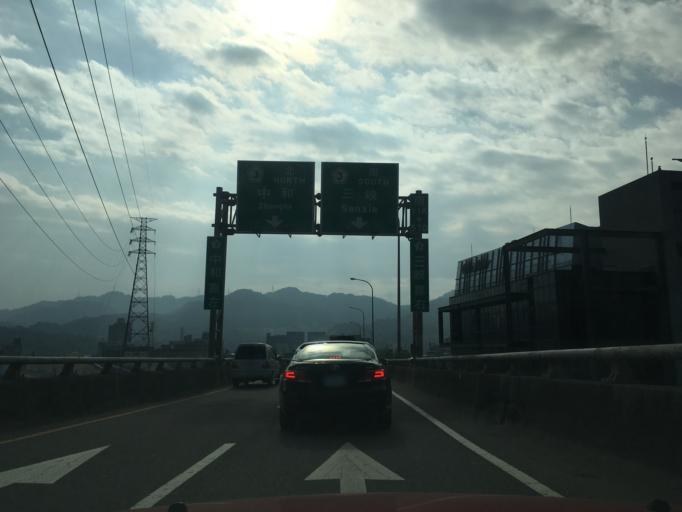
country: TW
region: Taipei
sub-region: Taipei
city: Banqiao
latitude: 24.9718
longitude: 121.4327
